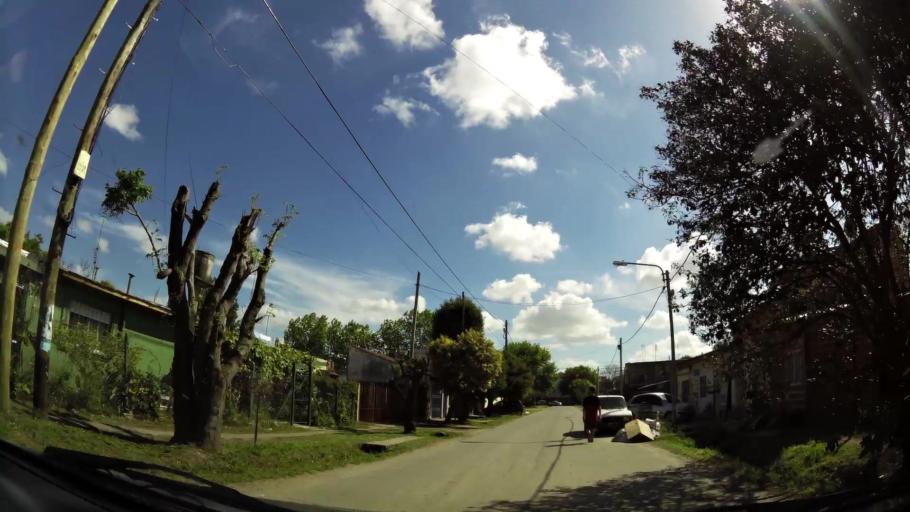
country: AR
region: Buenos Aires
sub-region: Partido de Quilmes
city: Quilmes
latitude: -34.8004
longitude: -58.2540
